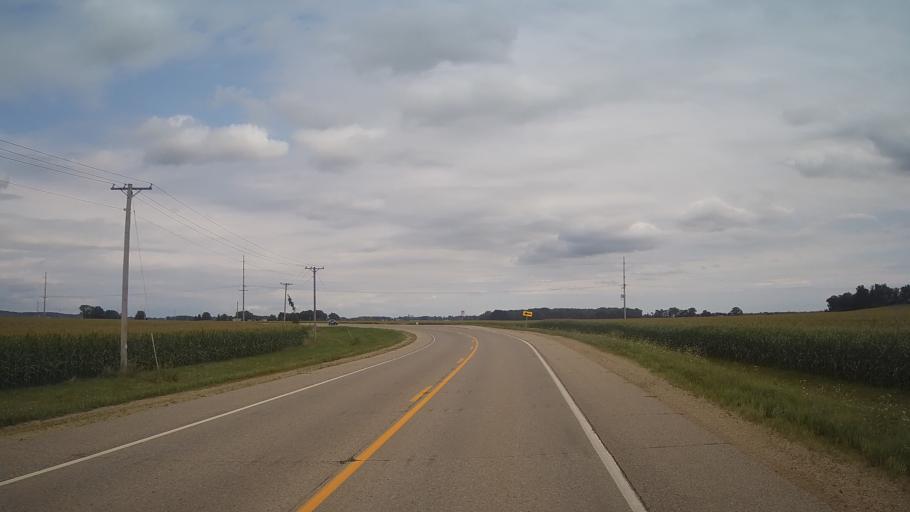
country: US
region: Wisconsin
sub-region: Waushara County
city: Redgranite
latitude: 44.0376
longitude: -89.0494
